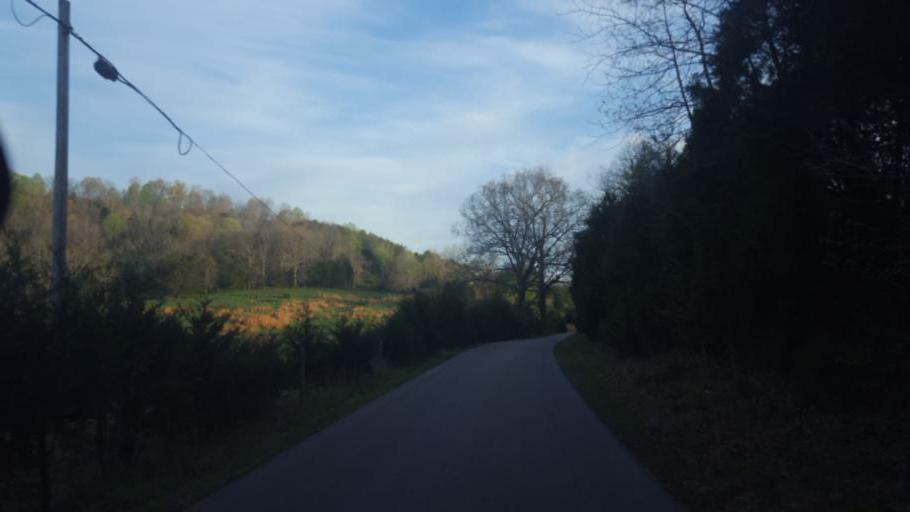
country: US
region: Kentucky
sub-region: Barren County
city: Cave City
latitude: 37.1858
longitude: -86.0115
